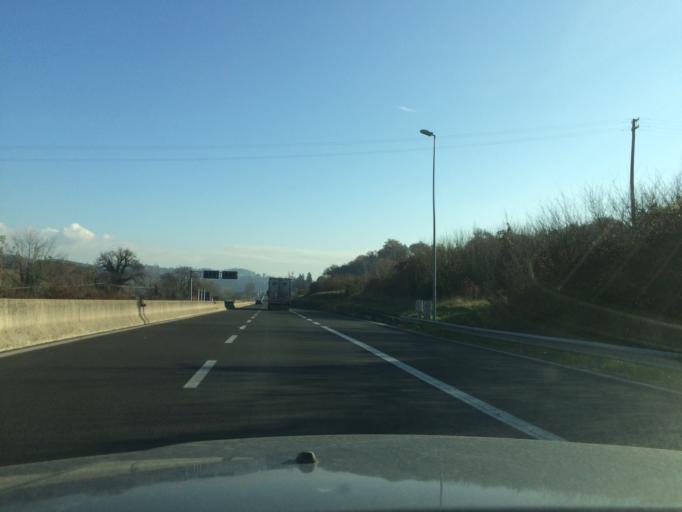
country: IT
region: Umbria
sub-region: Provincia di Perugia
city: Todi
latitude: 42.7859
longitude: 12.4310
